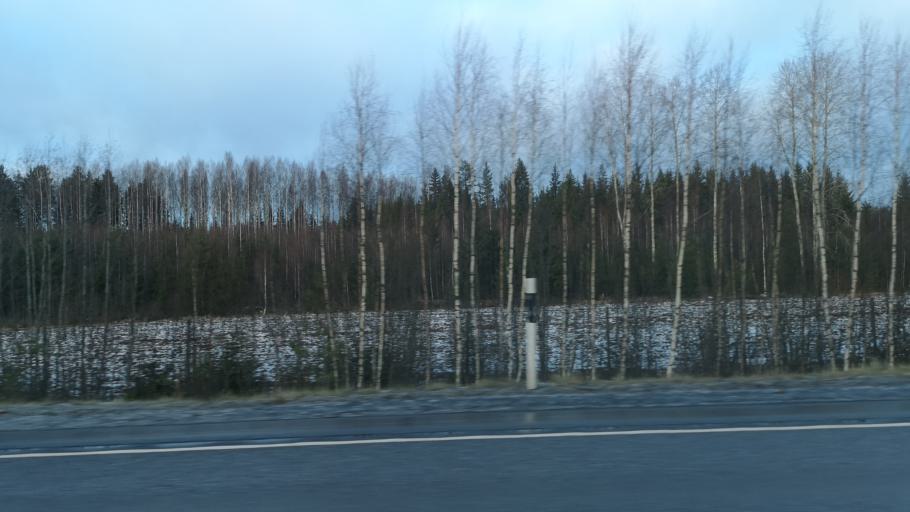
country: FI
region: Southern Savonia
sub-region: Mikkeli
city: Pertunmaa
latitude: 61.4061
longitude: 26.4023
